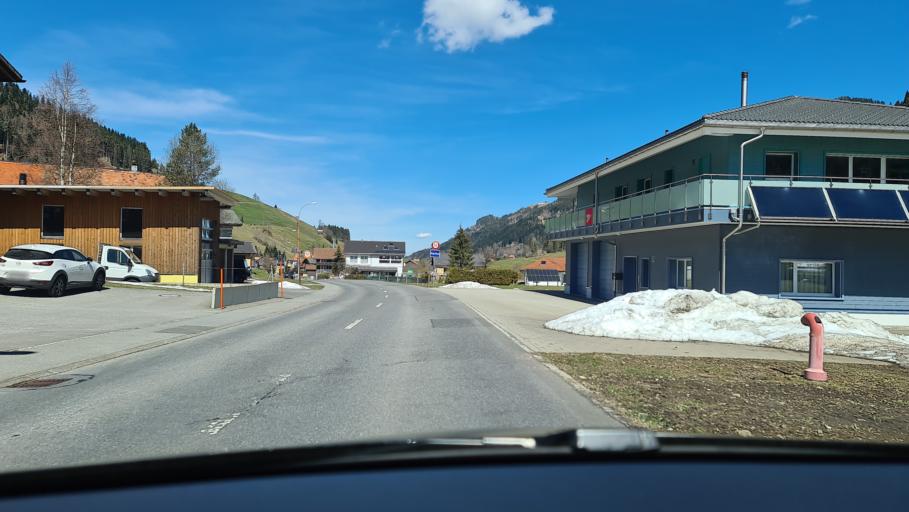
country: CH
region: Schwyz
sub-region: Bezirk Schwyz
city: Rothenthurm
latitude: 47.0639
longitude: 8.7139
